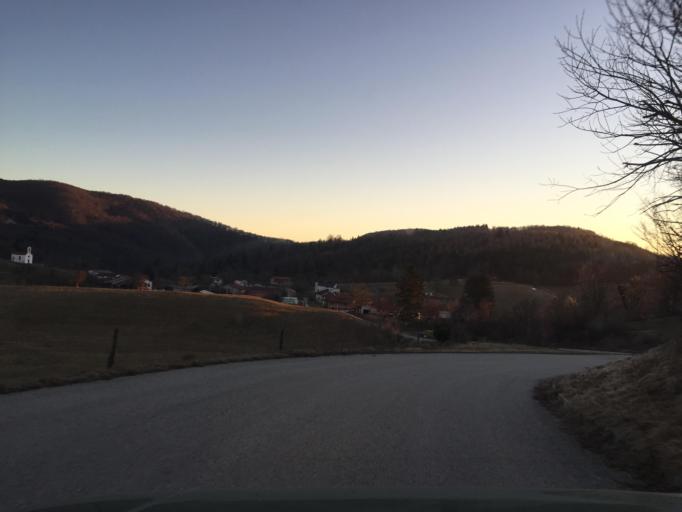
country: SI
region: Kanal
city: Kanal
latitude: 46.0809
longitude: 13.6621
